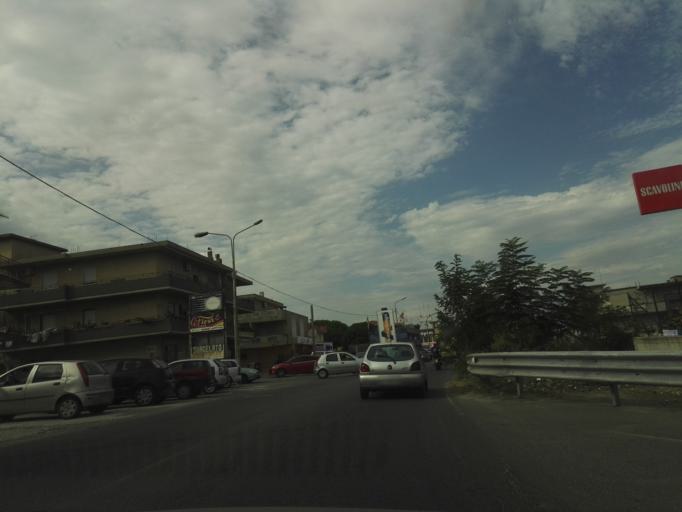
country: IT
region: Calabria
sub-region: Provincia di Catanzaro
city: Marina di Davoli
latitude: 38.6628
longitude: 16.5443
